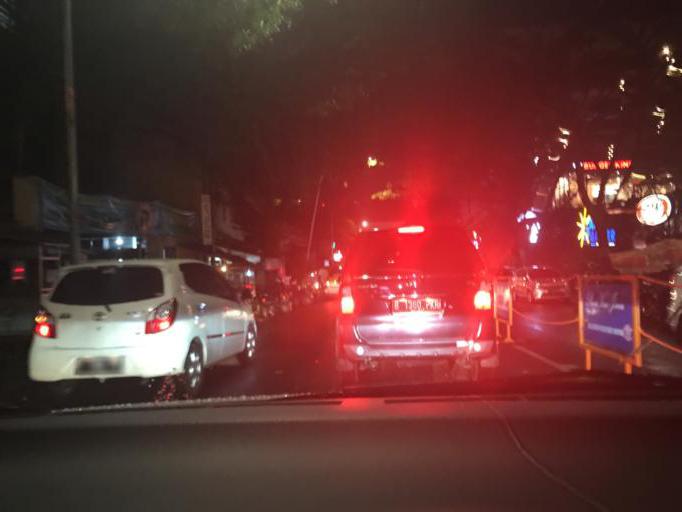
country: ID
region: West Java
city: Bandung
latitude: -6.8894
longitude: 107.5969
